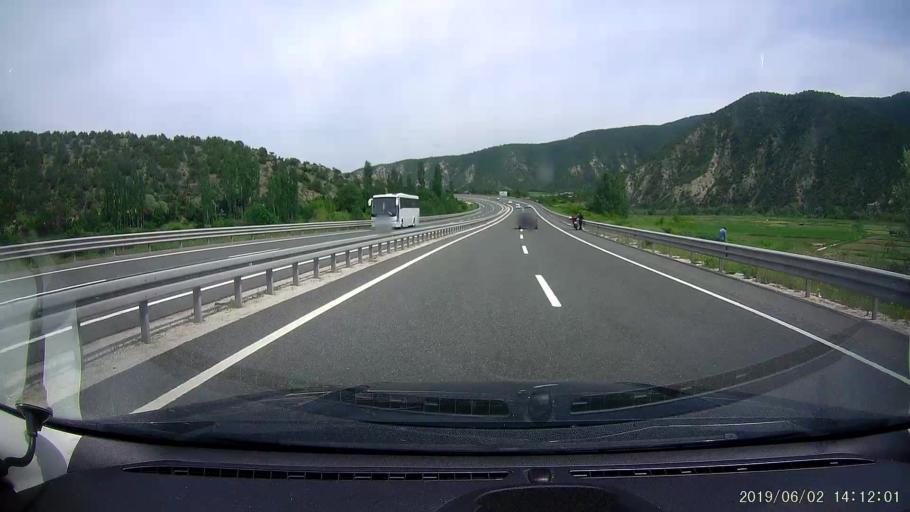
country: TR
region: Cankiri
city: Yaprakli
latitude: 40.9115
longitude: 33.8000
